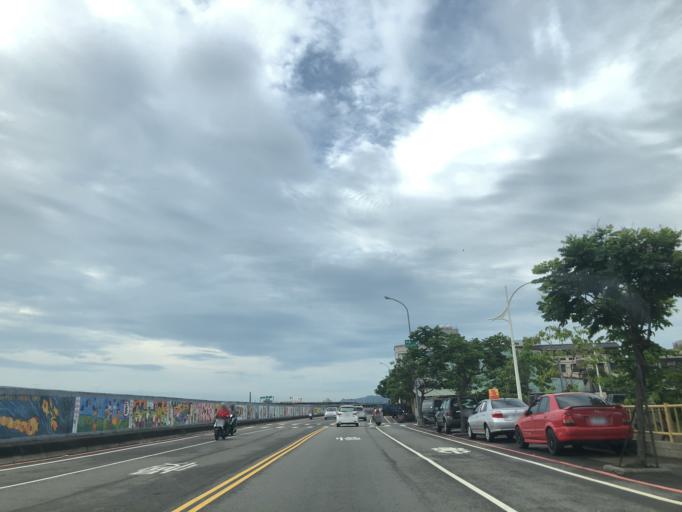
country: TW
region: Taiwan
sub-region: Taichung City
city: Taichung
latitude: 24.1049
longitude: 120.6959
